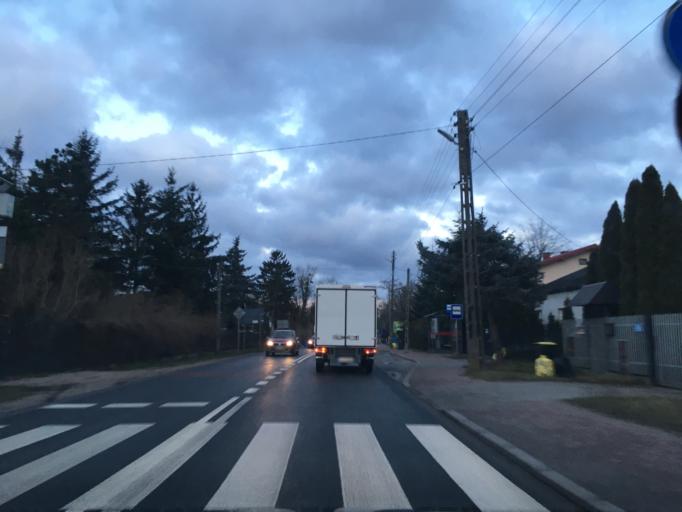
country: PL
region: Masovian Voivodeship
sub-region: Powiat grodziski
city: Milanowek
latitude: 52.0881
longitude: 20.6790
